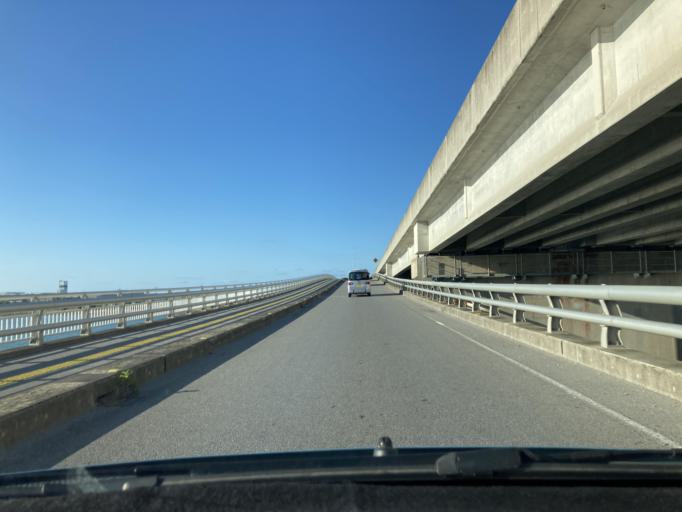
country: JP
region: Okinawa
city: Itoman
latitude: 26.1495
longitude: 127.6595
